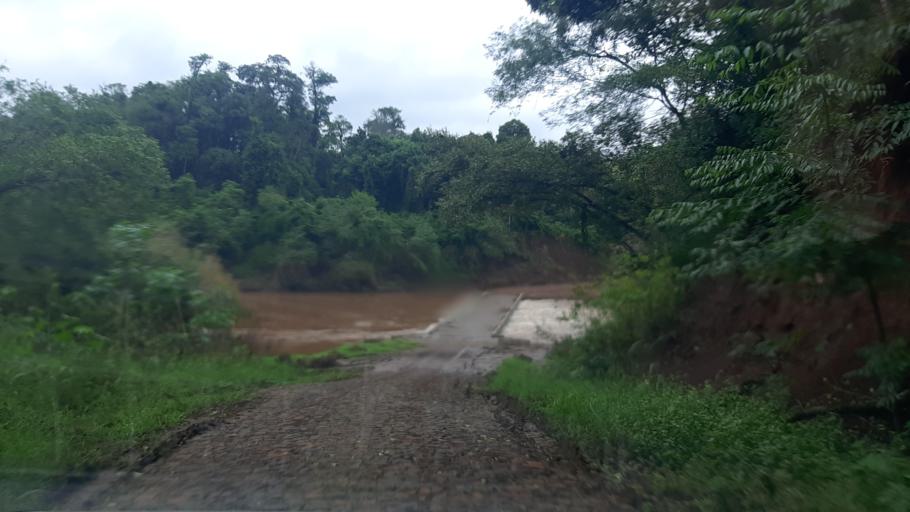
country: BR
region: Parana
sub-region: Ampere
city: Ampere
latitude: -26.0465
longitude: -53.5171
